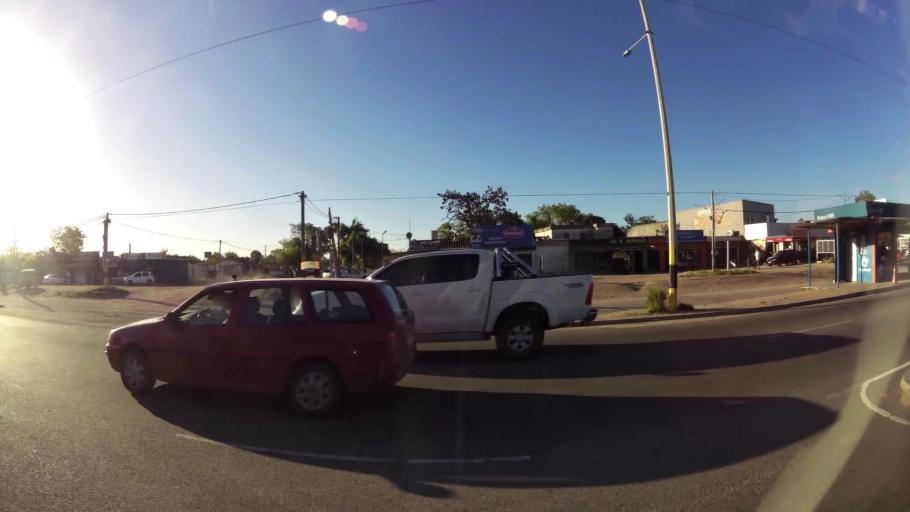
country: UY
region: Canelones
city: Paso de Carrasco
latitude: -34.8552
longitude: -56.0430
